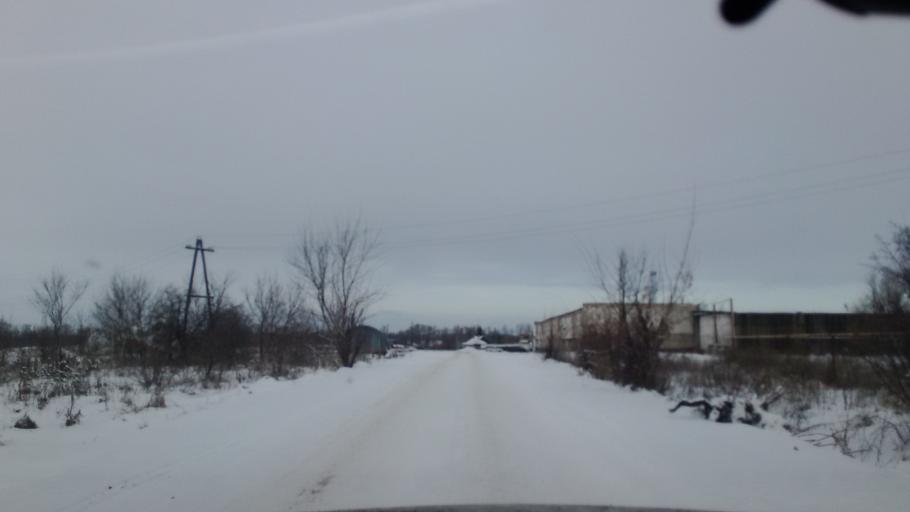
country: RU
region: Tula
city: Bogoroditsk
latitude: 53.7559
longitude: 38.1062
